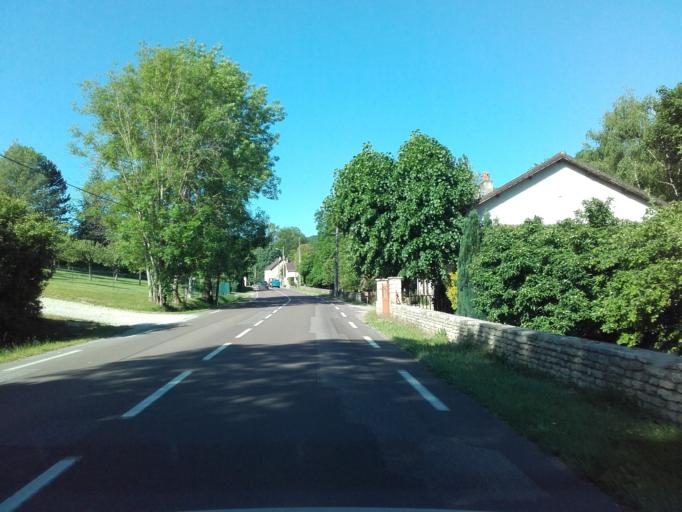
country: FR
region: Bourgogne
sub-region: Departement de la Cote-d'Or
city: Meursault
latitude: 46.9841
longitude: 4.7152
